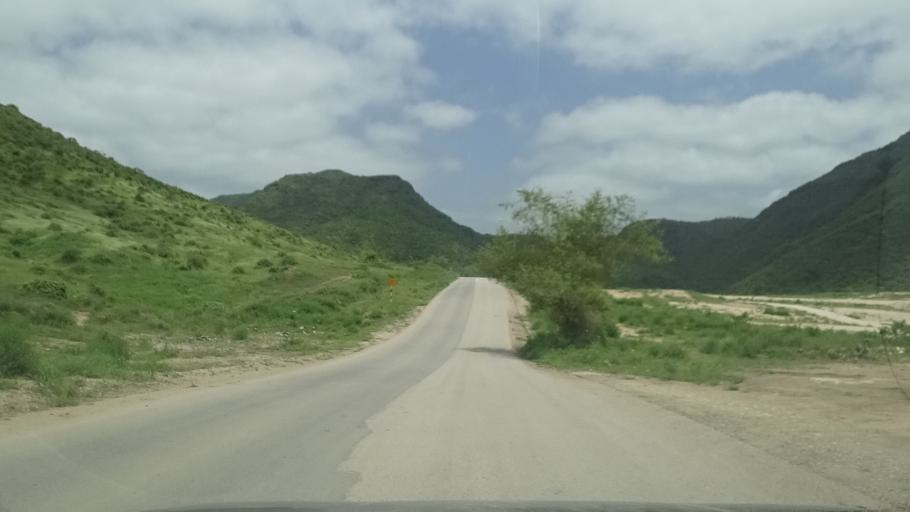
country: OM
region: Zufar
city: Salalah
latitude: 17.1455
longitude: 54.1757
